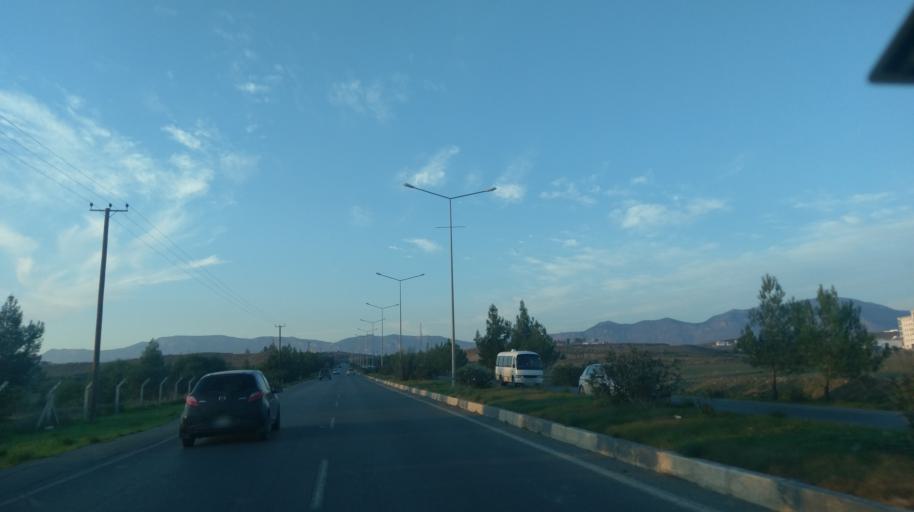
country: CY
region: Lefkosia
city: Nicosia
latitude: 35.2213
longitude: 33.3166
